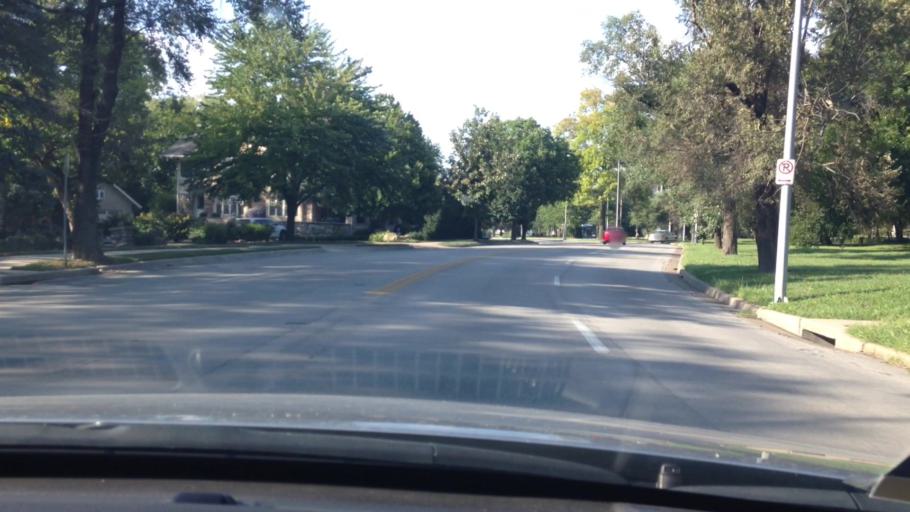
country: US
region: Kansas
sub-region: Johnson County
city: Westwood
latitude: 39.0308
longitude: -94.5844
